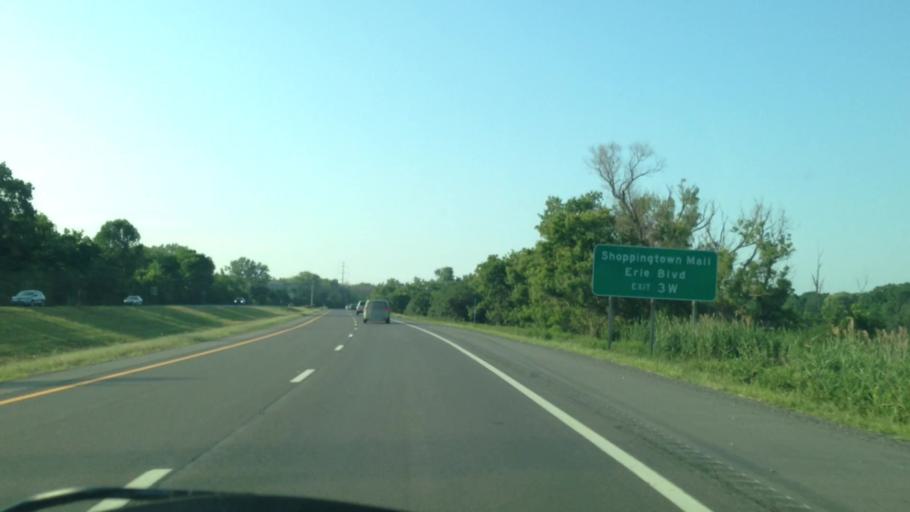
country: US
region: New York
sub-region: Onondaga County
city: East Syracuse
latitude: 43.0234
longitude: -76.0619
